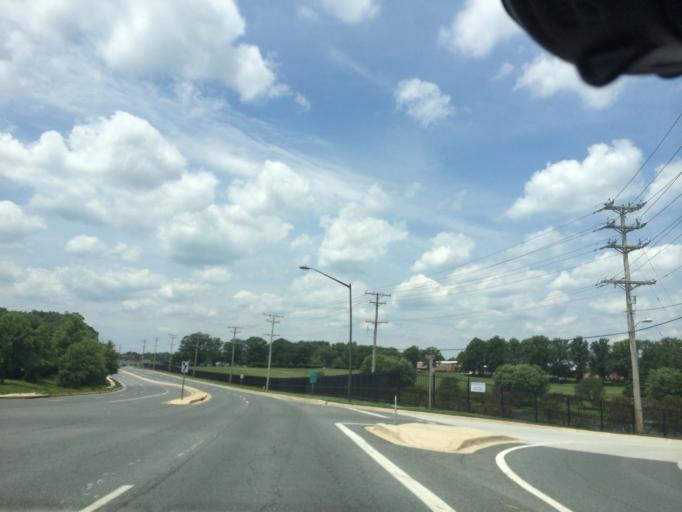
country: US
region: Maryland
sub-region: Howard County
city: Riverside
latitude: 39.1601
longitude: -76.8952
